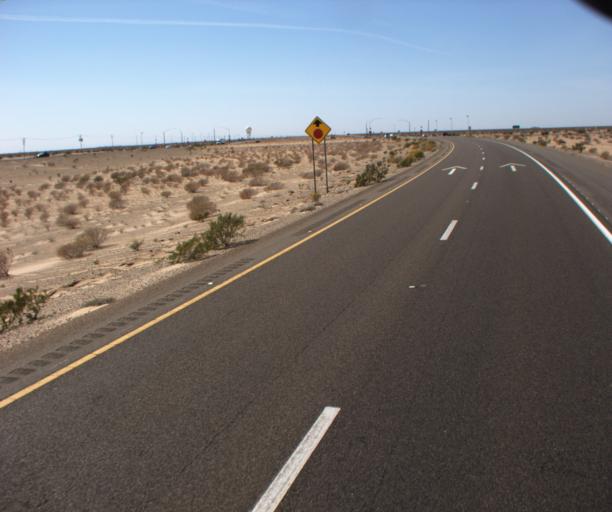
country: US
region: Arizona
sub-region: Yuma County
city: Somerton
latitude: 32.4965
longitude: -114.6442
